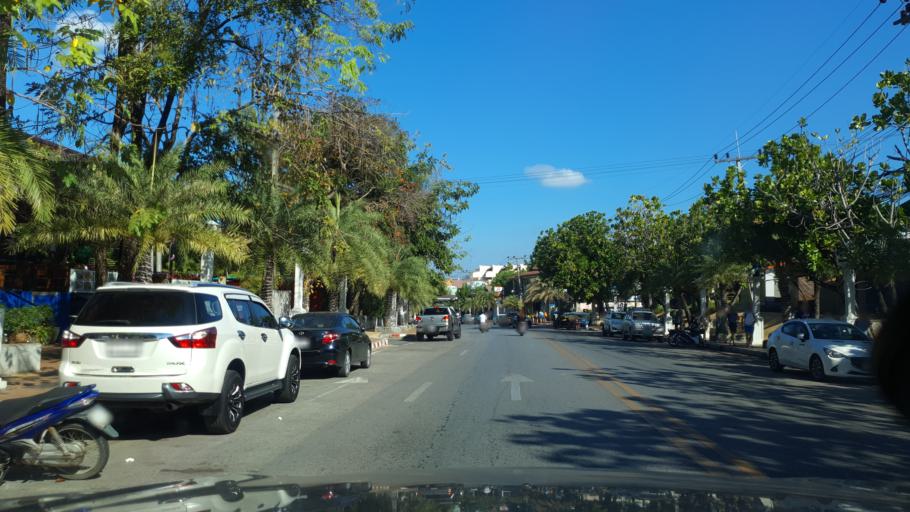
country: TH
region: Phangnga
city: Ban Ao Nang
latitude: 8.0367
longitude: 98.8187
